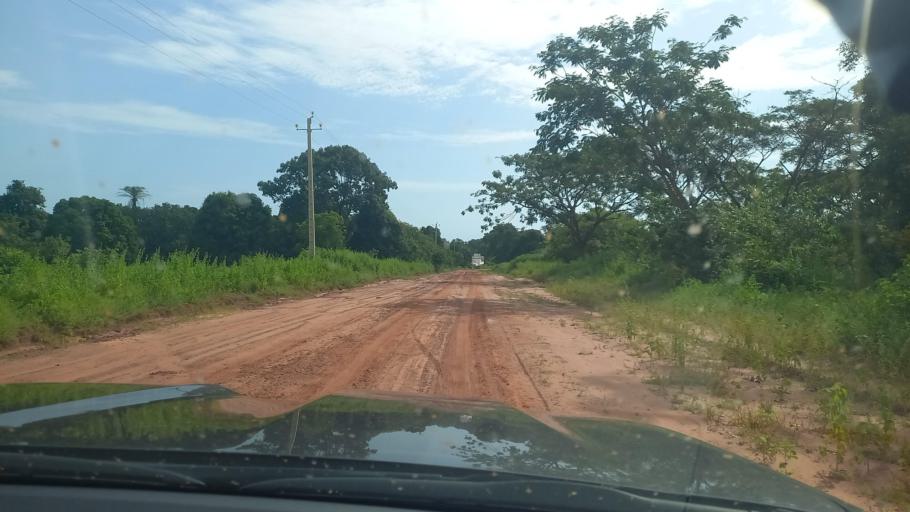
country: SN
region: Ziguinchor
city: Ziguinchor
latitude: 12.6722
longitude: -16.2127
